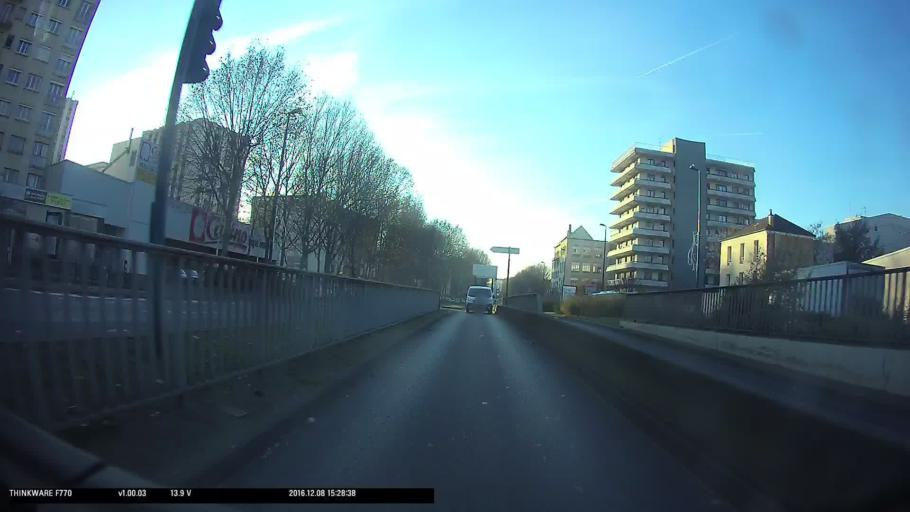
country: FR
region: Ile-de-France
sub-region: Departement de Seine-Saint-Denis
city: Romainville
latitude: 48.8953
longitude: 2.4248
